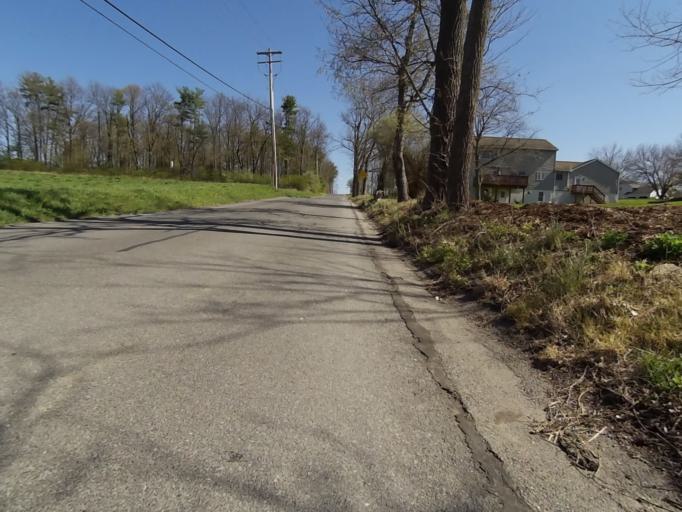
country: US
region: Pennsylvania
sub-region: Centre County
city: Bellefonte
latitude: 40.8852
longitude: -77.8254
